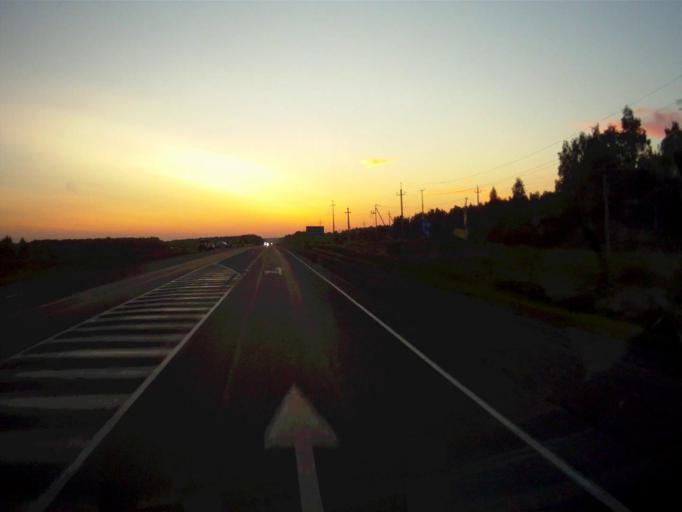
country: RU
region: Chelyabinsk
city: Poletayevo
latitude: 55.2144
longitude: 61.0592
